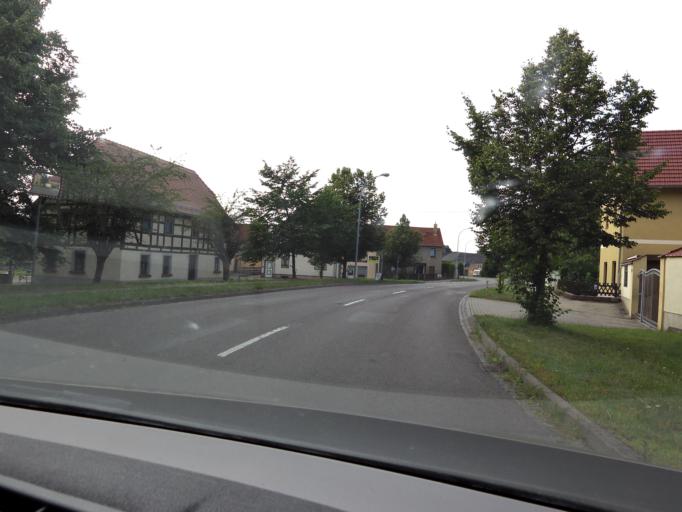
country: DE
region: Saxony
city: Otterwisch
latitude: 51.2380
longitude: 12.6139
